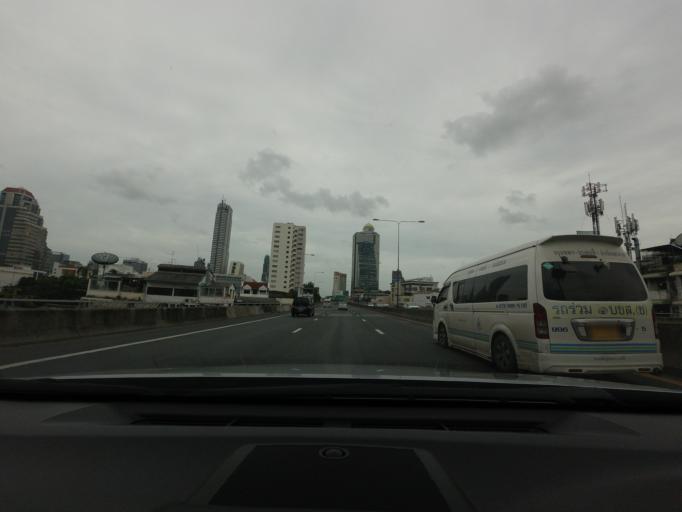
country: TH
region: Bangkok
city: Samphanthawong
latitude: 13.7287
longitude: 100.5175
